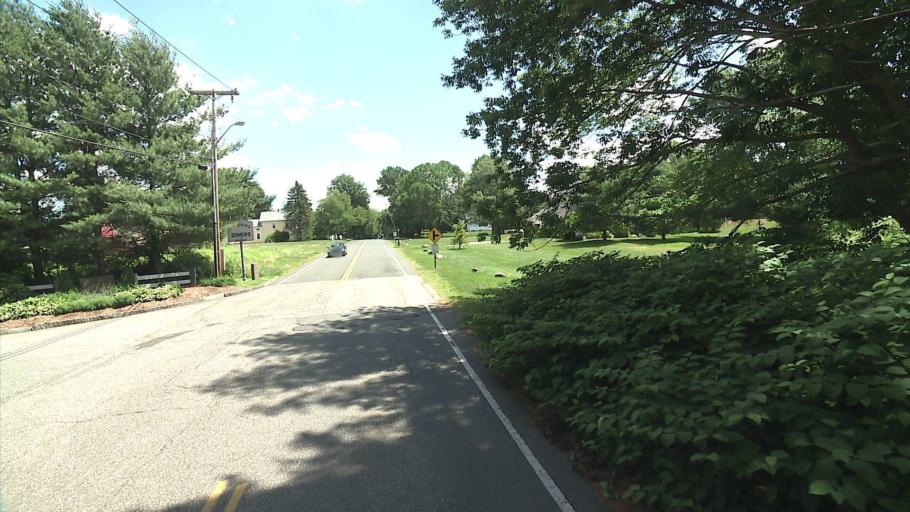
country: US
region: Massachusetts
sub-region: Hampden County
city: East Longmeadow
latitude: 42.0343
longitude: -72.4925
